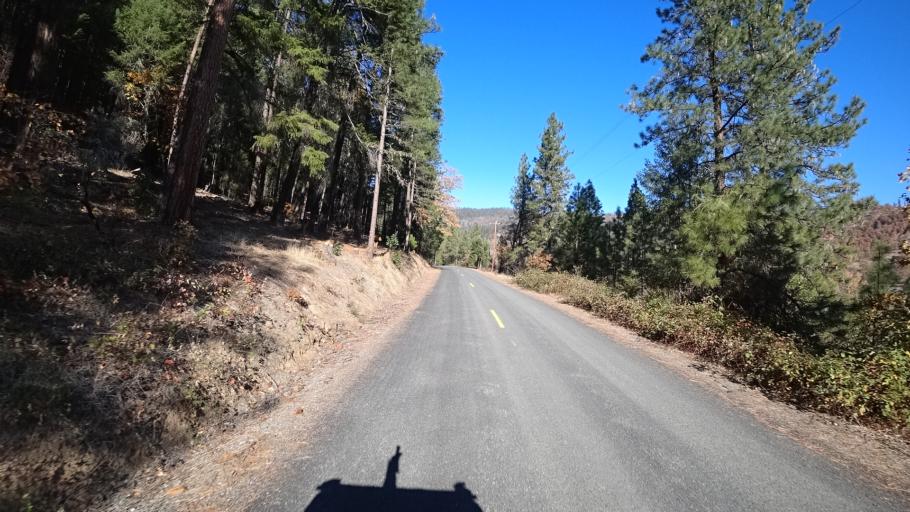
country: US
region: California
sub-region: Siskiyou County
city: Yreka
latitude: 41.8247
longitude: -122.9765
